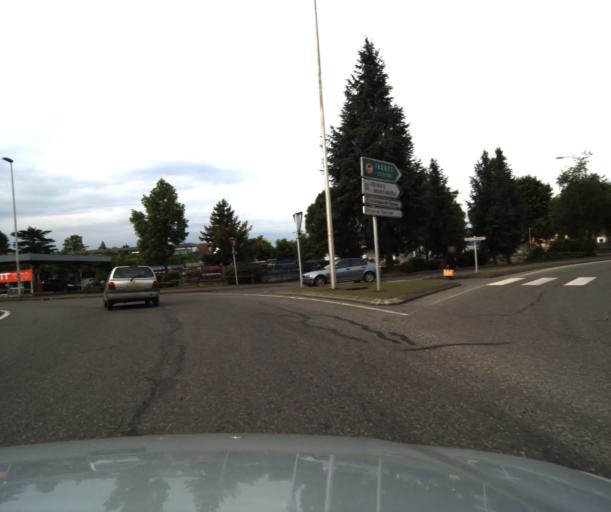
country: FR
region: Midi-Pyrenees
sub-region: Departement des Hautes-Pyrenees
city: Tarbes
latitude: 43.2288
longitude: 0.0883
